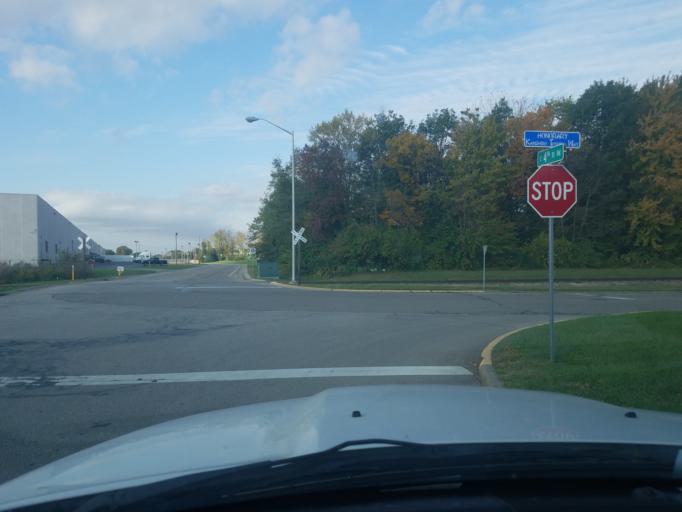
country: US
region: Indiana
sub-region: Jackson County
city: Seymour
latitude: 38.9669
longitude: -85.8620
